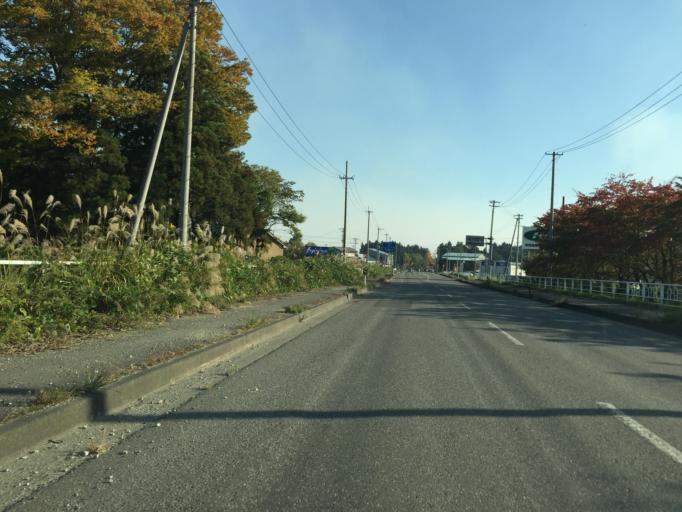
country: JP
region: Fukushima
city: Kitakata
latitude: 37.6731
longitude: 139.8886
